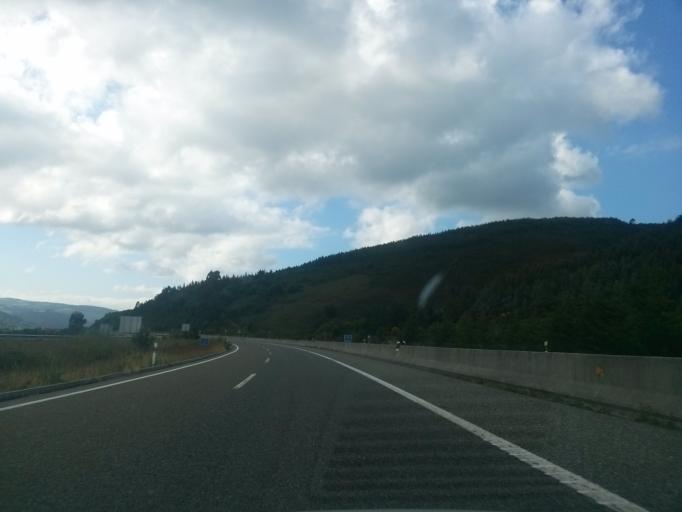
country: ES
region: Galicia
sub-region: Provincia de Lugo
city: Becerrea
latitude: 42.8843
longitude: -7.1770
